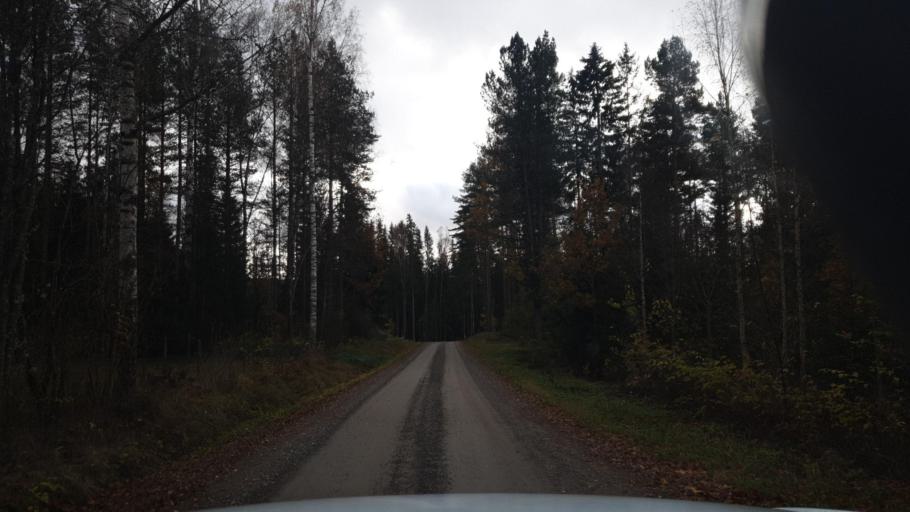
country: SE
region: Vaermland
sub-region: Arvika Kommun
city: Arvika
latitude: 59.5080
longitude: 12.7314
